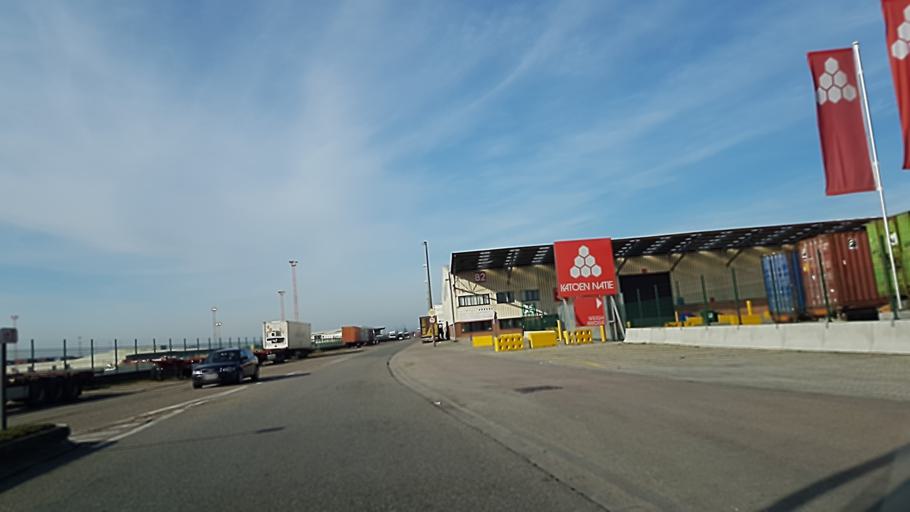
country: BE
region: Flanders
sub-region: Provincie Antwerpen
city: Stabroek
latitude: 51.3265
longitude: 4.3457
